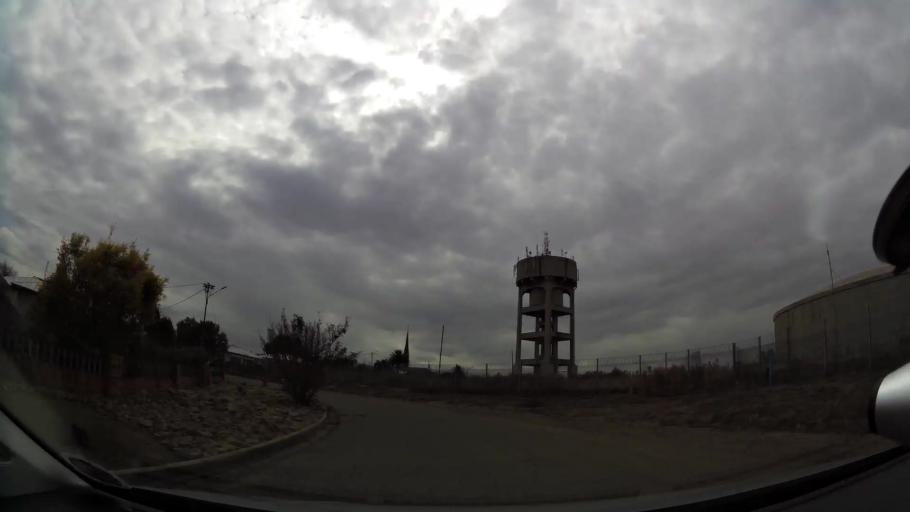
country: ZA
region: Orange Free State
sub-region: Fezile Dabi District Municipality
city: Kroonstad
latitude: -27.6512
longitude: 27.2333
